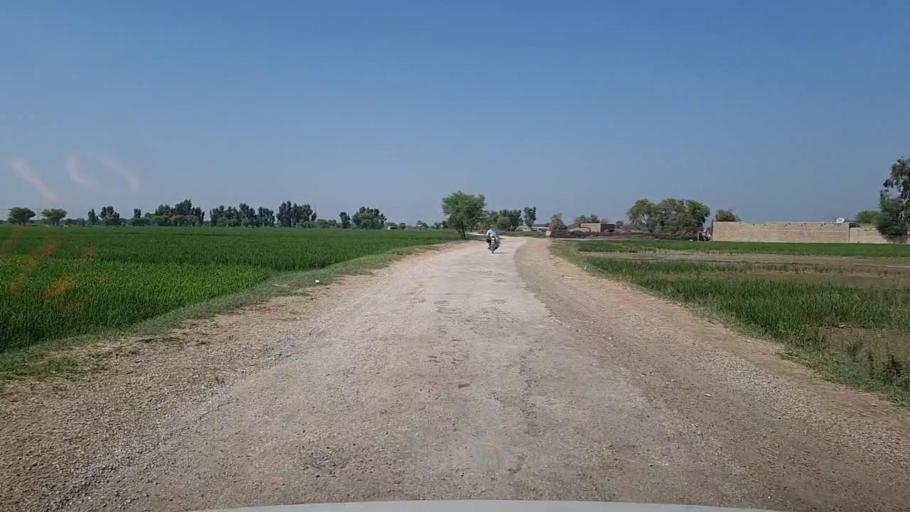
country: PK
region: Sindh
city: Kandhkot
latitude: 28.3284
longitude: 69.3670
